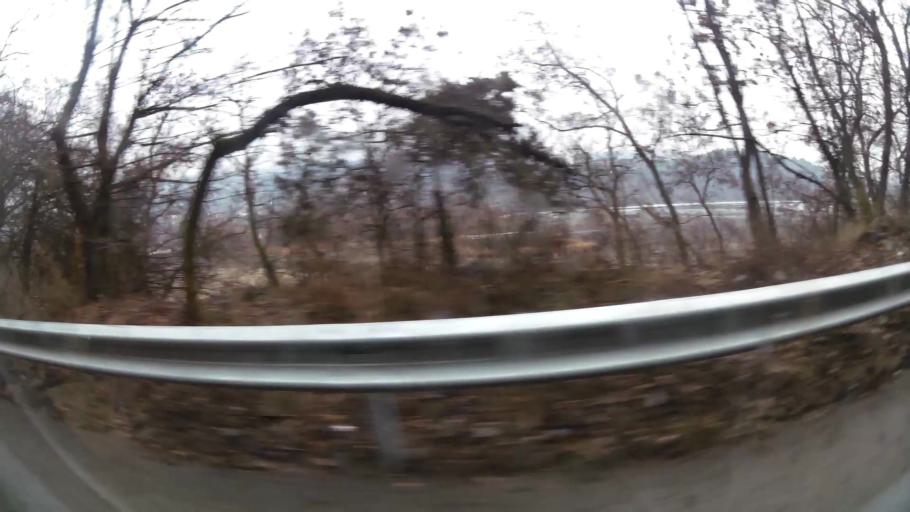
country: BG
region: Sofia-Capital
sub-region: Stolichna Obshtina
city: Sofia
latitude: 42.5903
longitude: 23.4246
